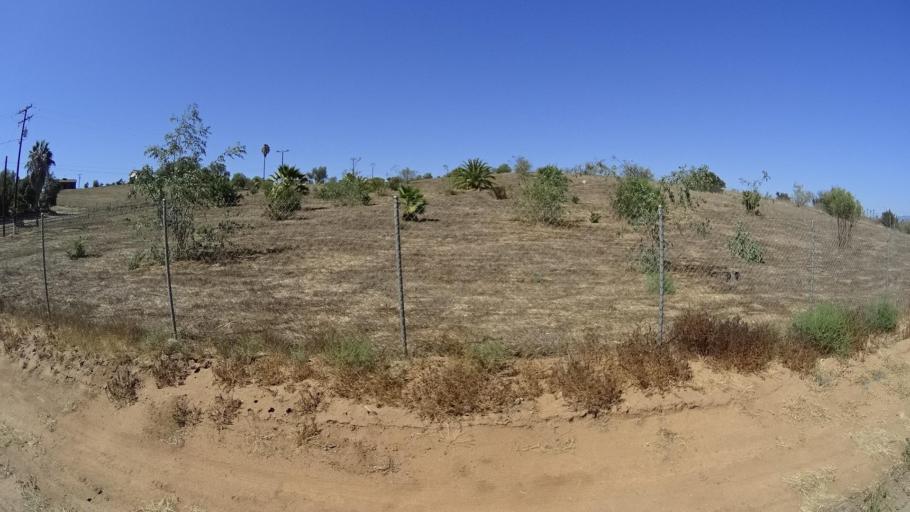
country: US
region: California
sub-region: San Diego County
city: Bonsall
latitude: 33.2928
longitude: -117.1852
